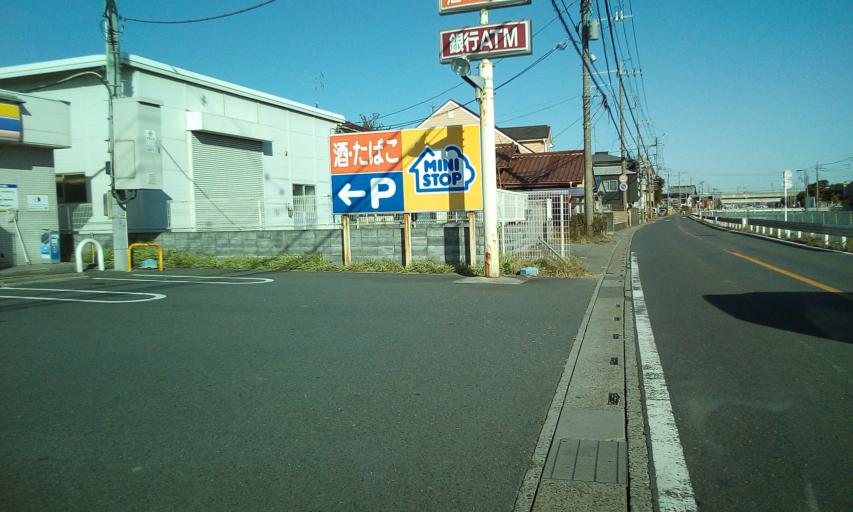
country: JP
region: Chiba
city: Nagareyama
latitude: 35.8254
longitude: 139.8829
